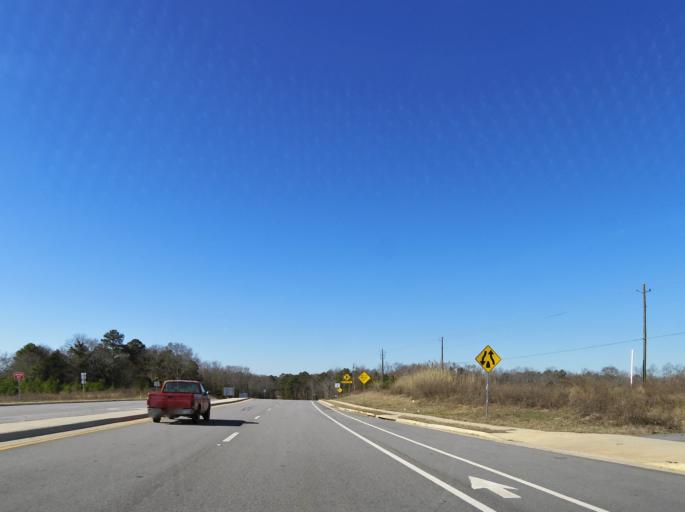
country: US
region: Georgia
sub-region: Peach County
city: Byron
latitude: 32.7165
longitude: -83.7327
